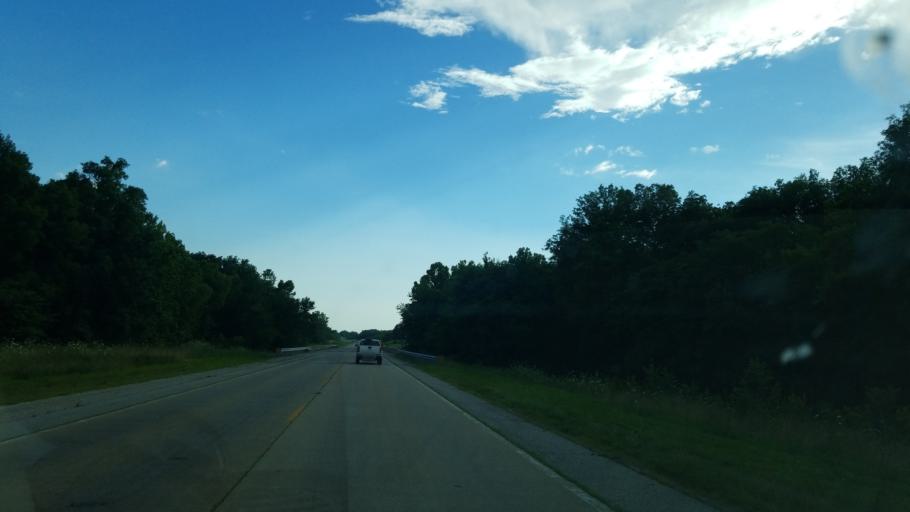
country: US
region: Illinois
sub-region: Marion County
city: Central City
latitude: 38.5642
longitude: -89.1180
